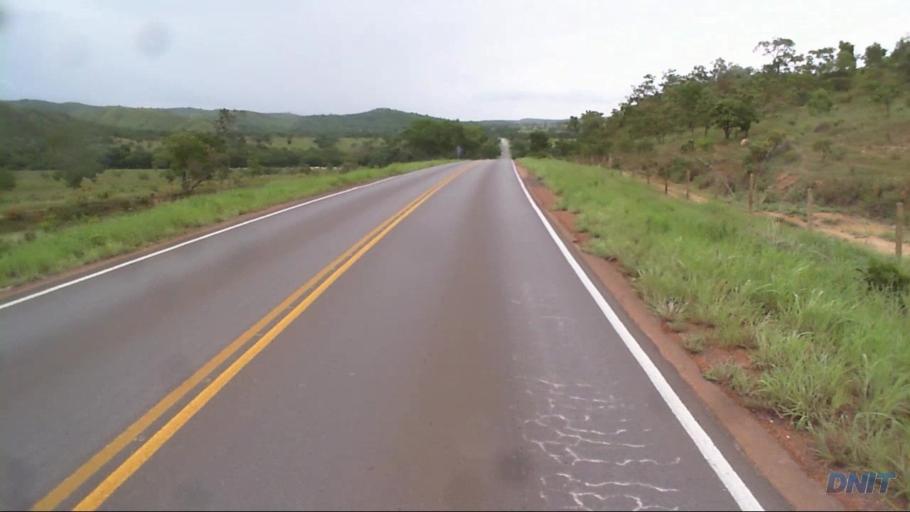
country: BR
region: Goias
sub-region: Padre Bernardo
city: Padre Bernardo
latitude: -15.4395
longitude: -48.1949
